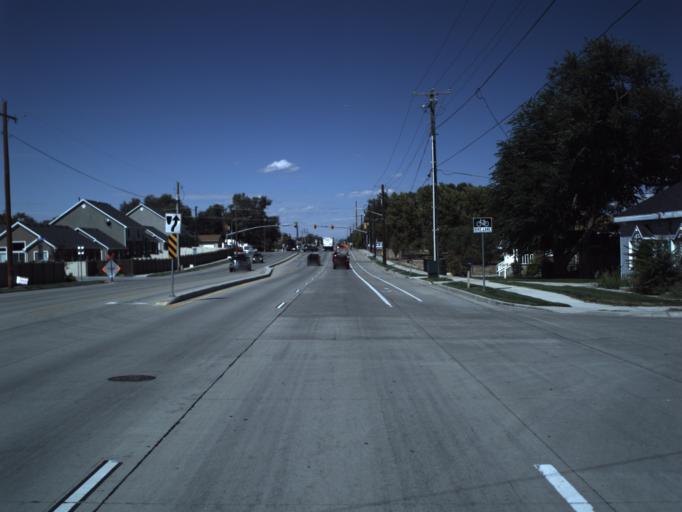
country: US
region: Utah
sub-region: Salt Lake County
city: Riverton
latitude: 40.5348
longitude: -111.9386
